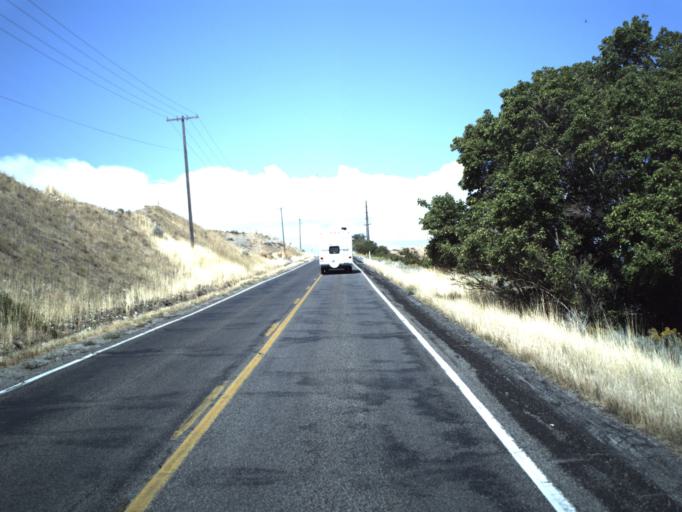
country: US
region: Utah
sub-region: Cache County
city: Hyrum
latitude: 41.6310
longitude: -111.8105
